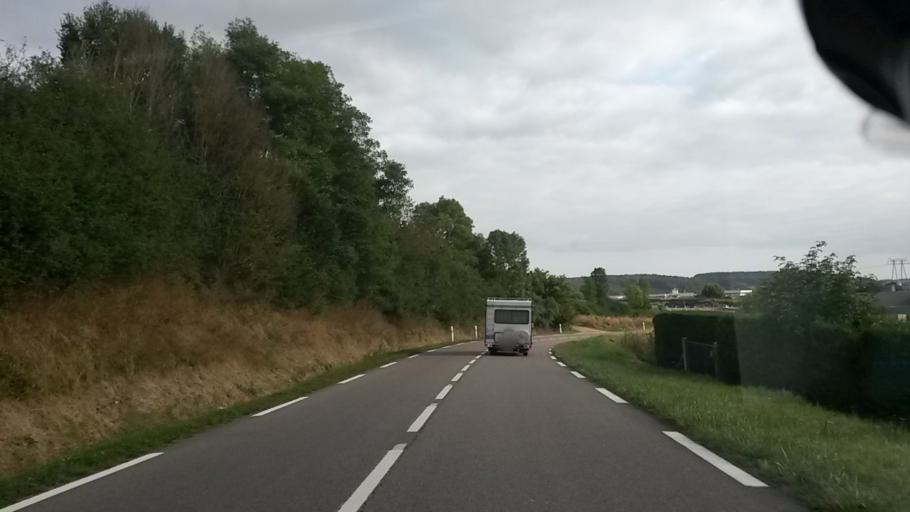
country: FR
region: Haute-Normandie
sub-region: Departement de l'Eure
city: Gravigny
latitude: 49.0634
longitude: 1.1746
